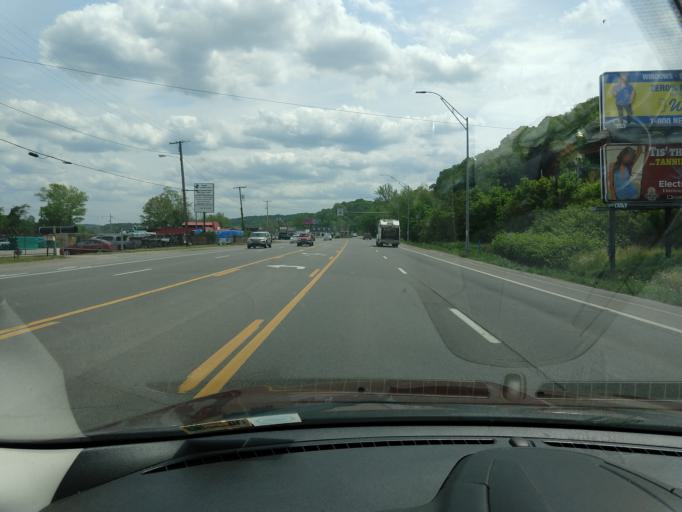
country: US
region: West Virginia
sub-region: Kanawha County
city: Dunbar
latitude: 38.3608
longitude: -81.7591
